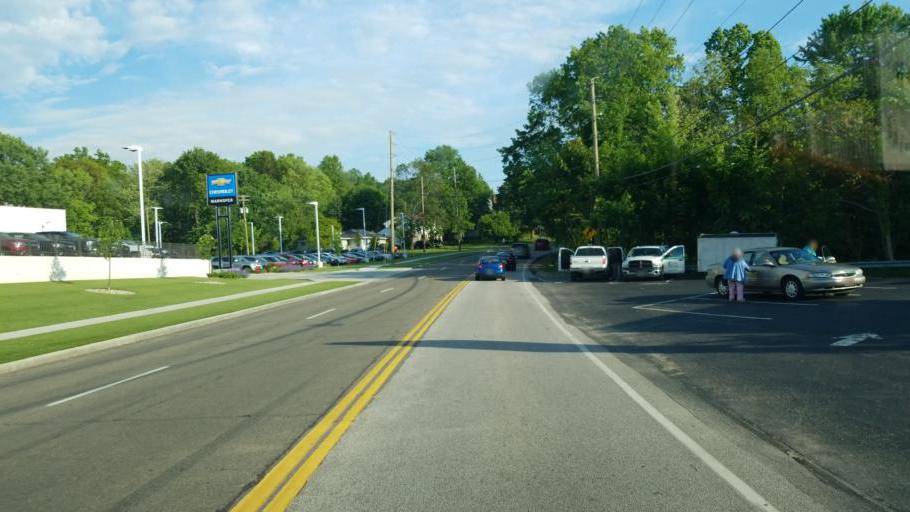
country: US
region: Ohio
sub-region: Summit County
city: Stow
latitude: 41.1586
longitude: -81.4402
